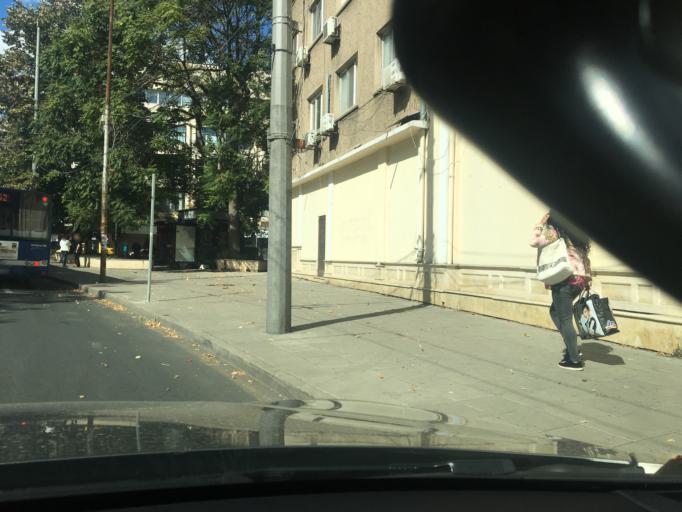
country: BG
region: Burgas
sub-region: Obshtina Burgas
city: Burgas
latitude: 42.4929
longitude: 27.4712
